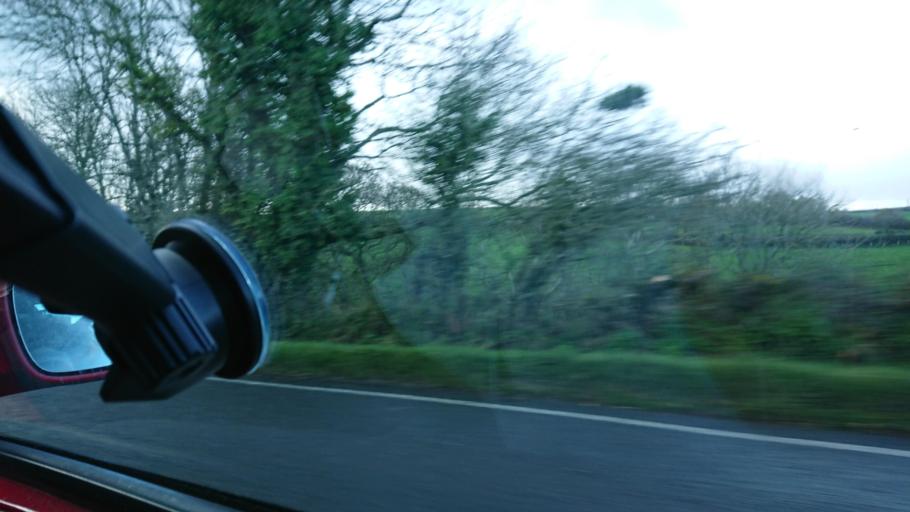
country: GB
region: England
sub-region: Cornwall
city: Looe
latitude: 50.3496
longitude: -4.4773
